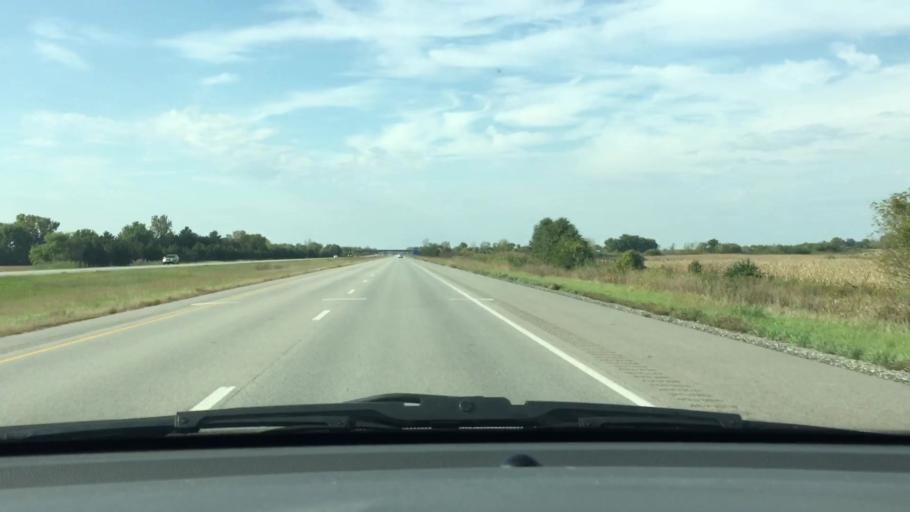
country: US
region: Illinois
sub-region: Rock Island County
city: Port Byron
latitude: 41.5785
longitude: -90.2137
